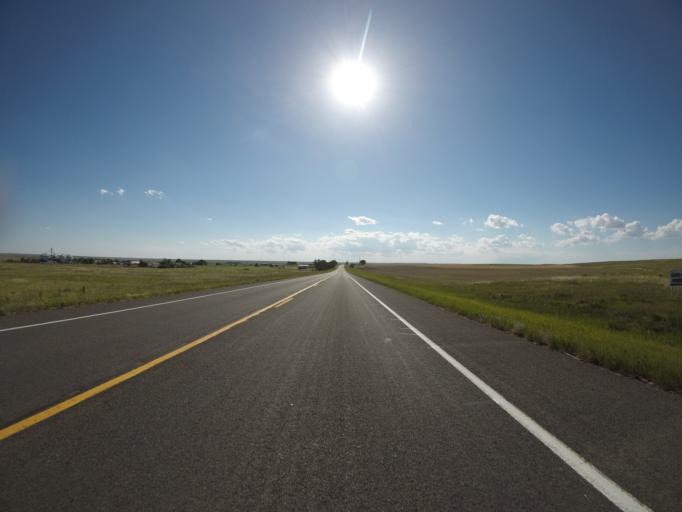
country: US
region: Colorado
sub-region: Morgan County
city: Brush
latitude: 40.6101
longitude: -103.6593
